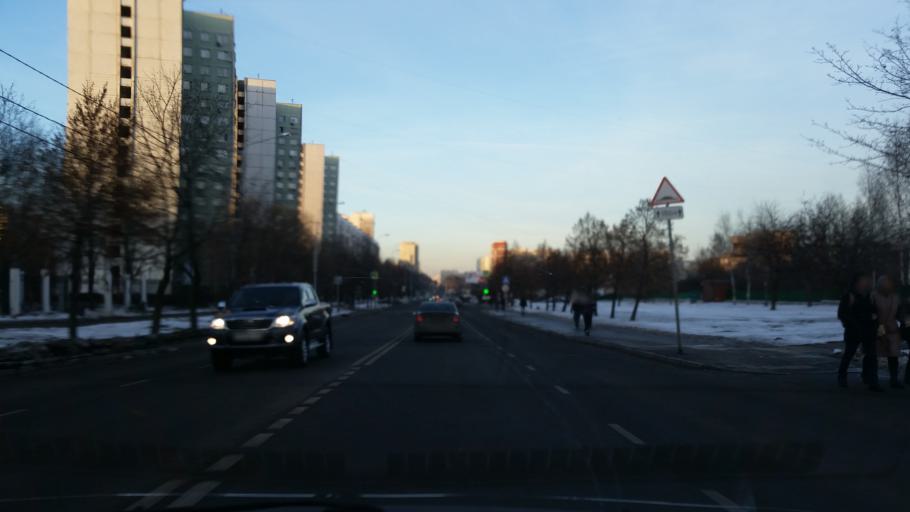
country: RU
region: Moscow
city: Chertanovo Yuzhnoye
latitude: 55.6157
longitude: 37.6056
